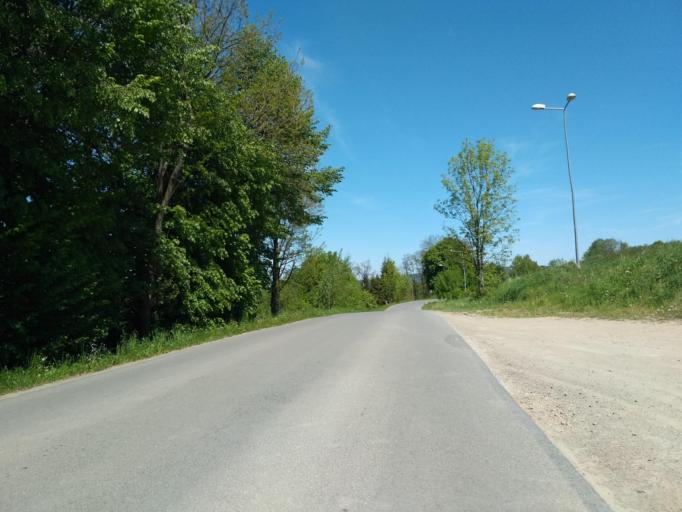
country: PL
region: Subcarpathian Voivodeship
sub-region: Powiat sanocki
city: Nowosielce-Gniewosz
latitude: 49.5331
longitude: 22.0512
